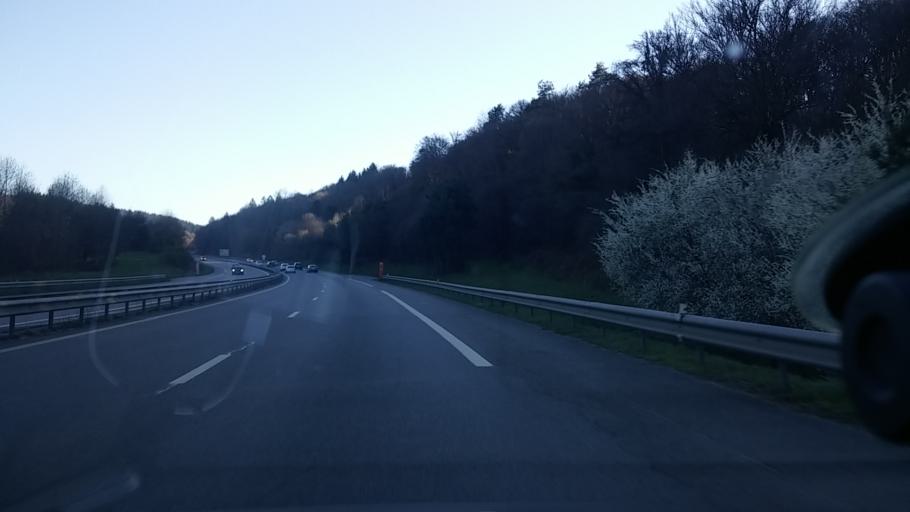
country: FR
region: Limousin
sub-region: Departement de la Haute-Vienne
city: Razes
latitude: 46.0397
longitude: 1.3499
